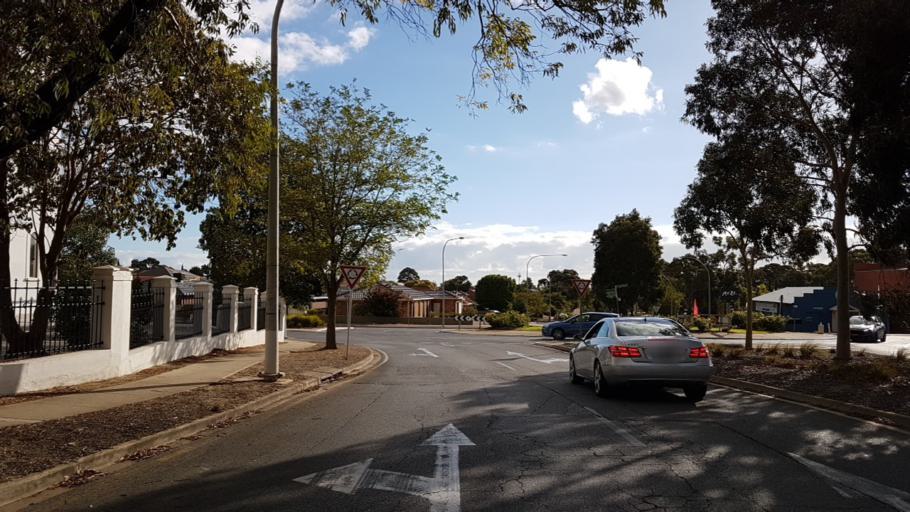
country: AU
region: South Australia
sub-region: Campbelltown
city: Athelstone
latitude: -34.8778
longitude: 138.6915
